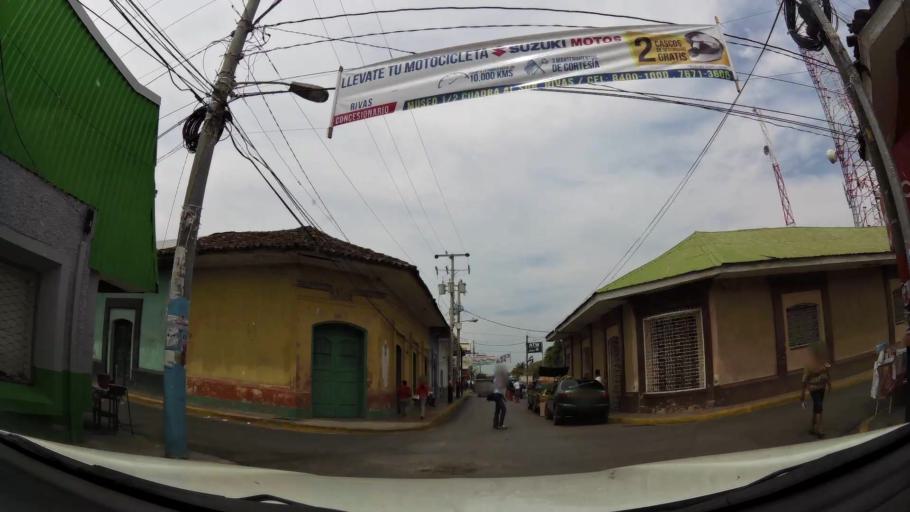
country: NI
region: Rivas
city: Rivas
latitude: 11.4390
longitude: -85.8297
